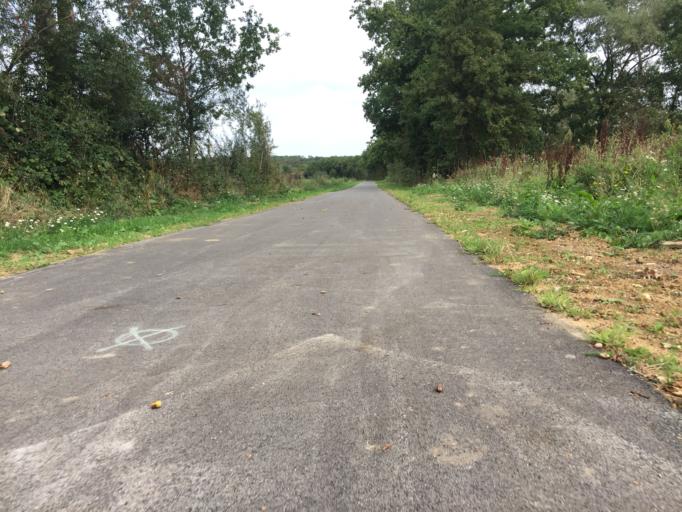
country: FR
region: Picardie
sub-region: Departement de l'Oise
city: Auneuil
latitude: 49.3925
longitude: 2.0098
